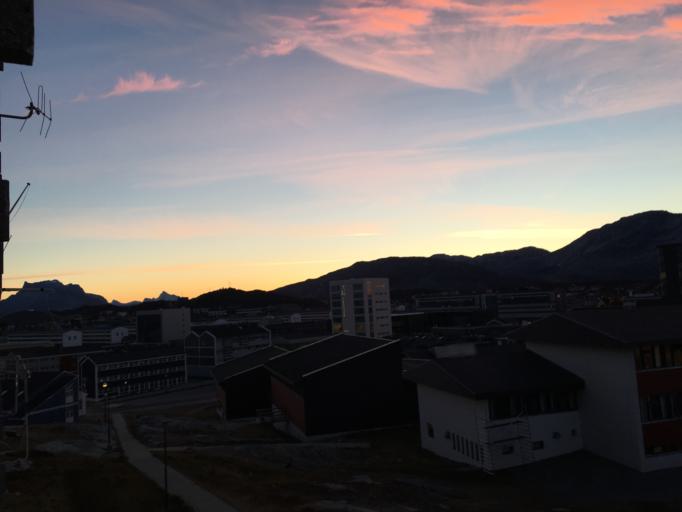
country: GL
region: Sermersooq
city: Nuuk
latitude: 64.1746
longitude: -51.7437
